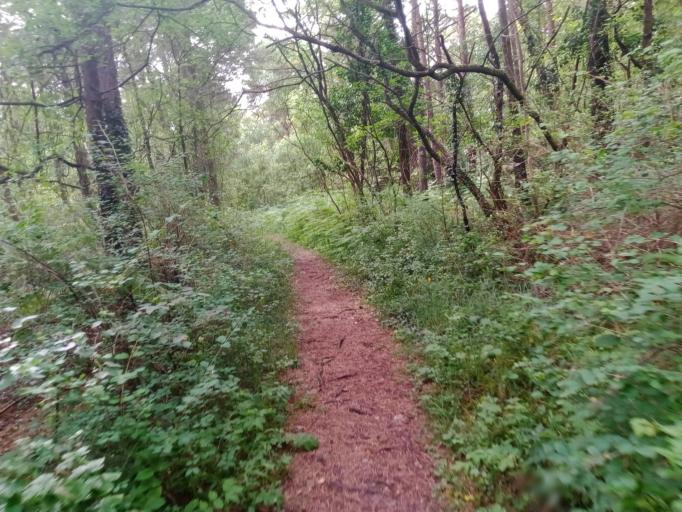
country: IE
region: Leinster
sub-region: Laois
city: Abbeyleix
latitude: 52.8859
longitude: -7.3582
